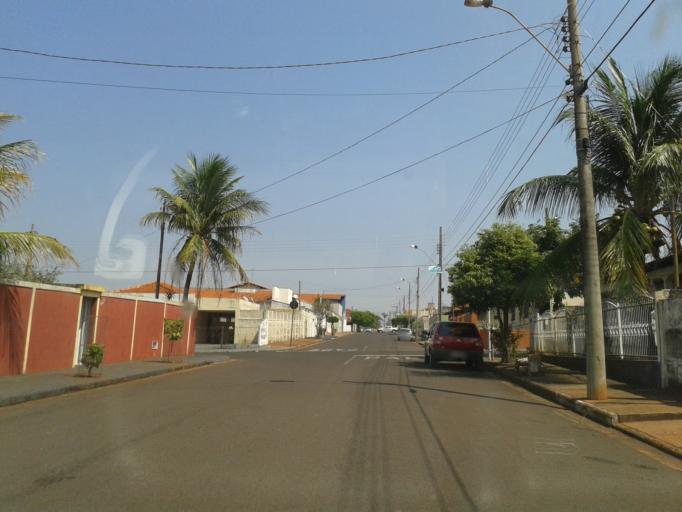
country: BR
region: Minas Gerais
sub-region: Ituiutaba
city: Ituiutaba
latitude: -18.9758
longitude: -49.4736
